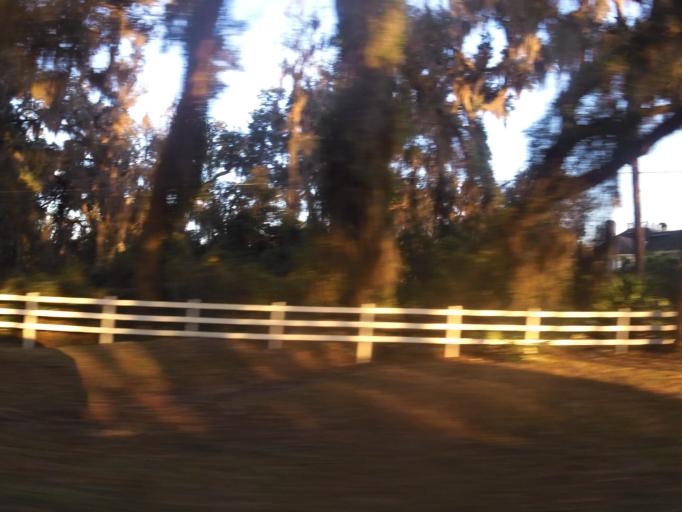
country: US
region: Florida
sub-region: Clay County
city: Green Cove Springs
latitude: 29.9098
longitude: -81.5922
